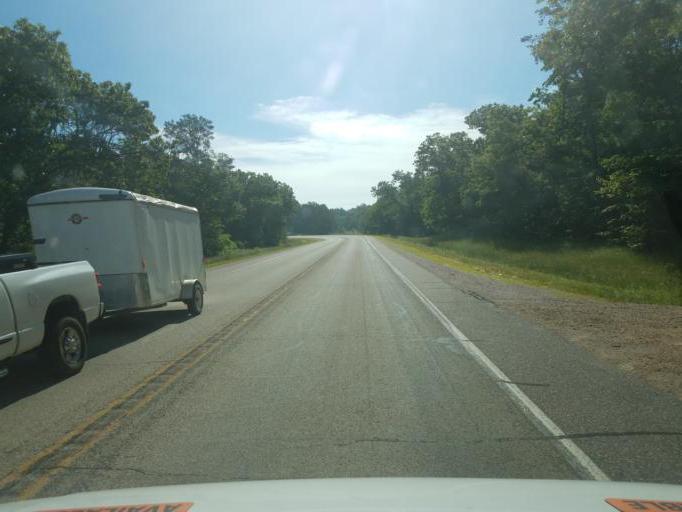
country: US
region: Wisconsin
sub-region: Sauk County
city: Lake Delton
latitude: 43.5687
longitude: -89.8297
